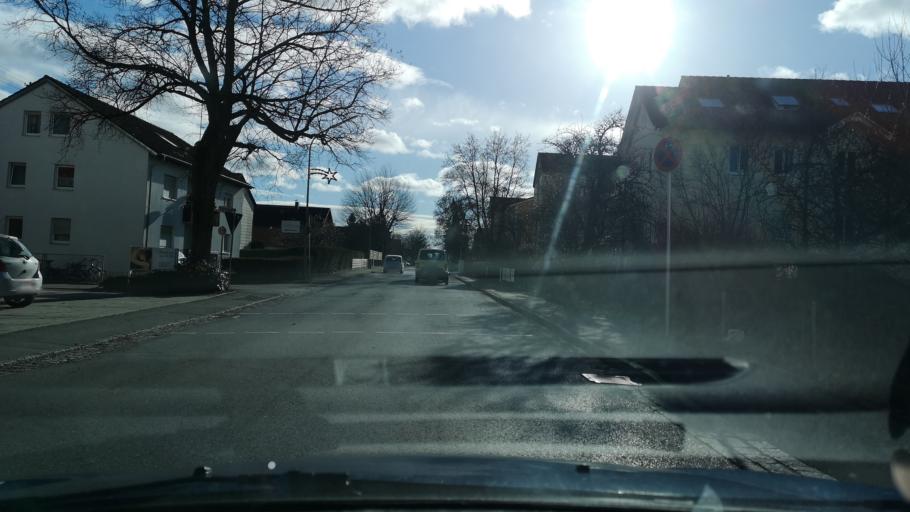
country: DE
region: Bavaria
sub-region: Upper Bavaria
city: Poing
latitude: 48.1688
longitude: 11.8120
